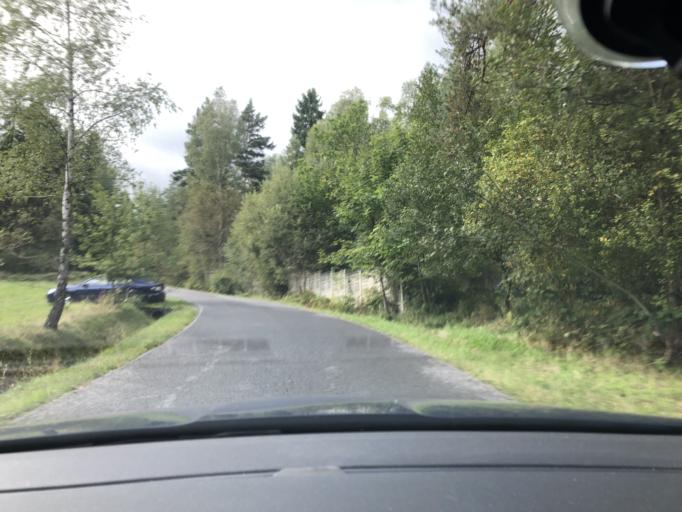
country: PL
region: Silesian Voivodeship
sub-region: Powiat zywiecki
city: Slemien
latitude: 49.7182
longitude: 19.4182
